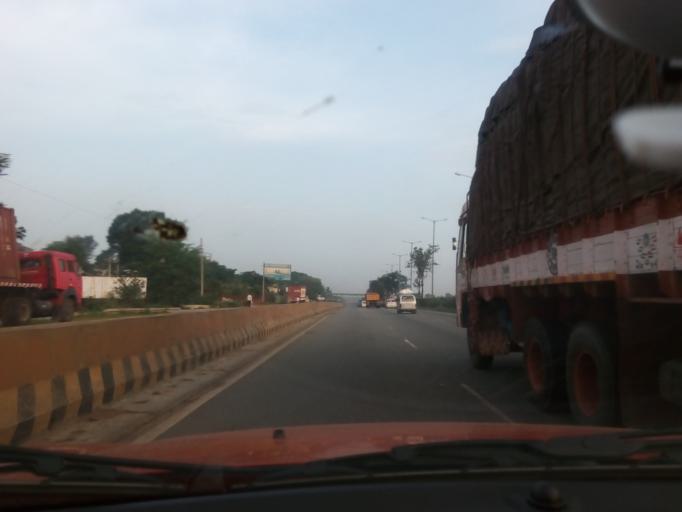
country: IN
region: Karnataka
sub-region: Bangalore Rural
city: Nelamangala
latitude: 13.0869
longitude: 77.4086
